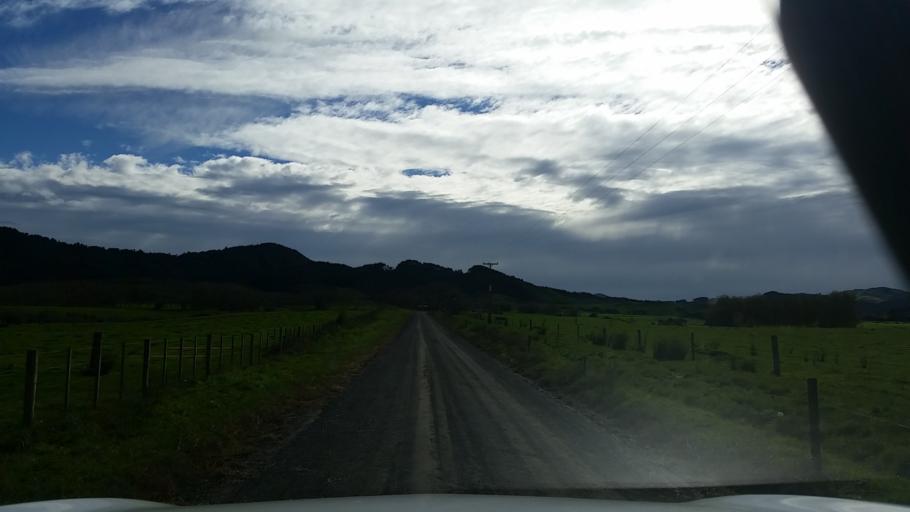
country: NZ
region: Waikato
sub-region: Hauraki District
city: Ngatea
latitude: -37.5109
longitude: 175.4084
